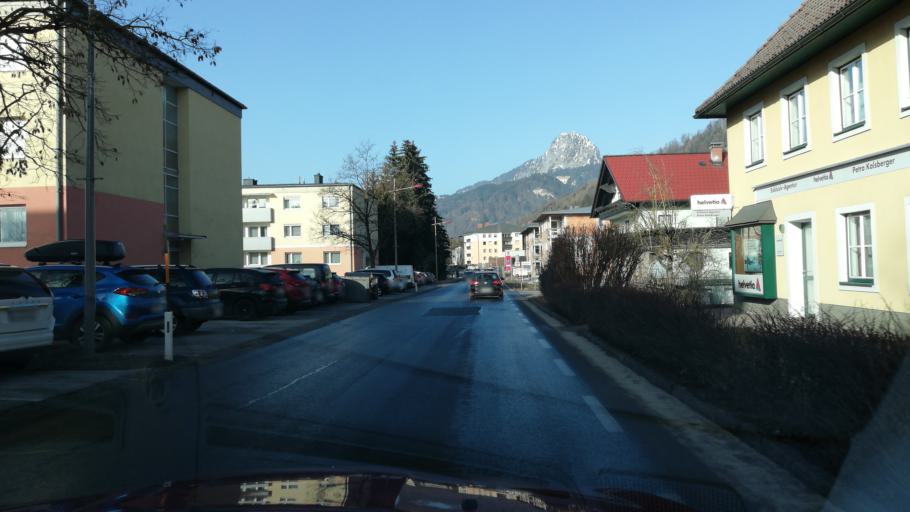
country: AT
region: Styria
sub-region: Politischer Bezirk Liezen
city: Liezen
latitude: 47.5697
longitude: 14.2358
